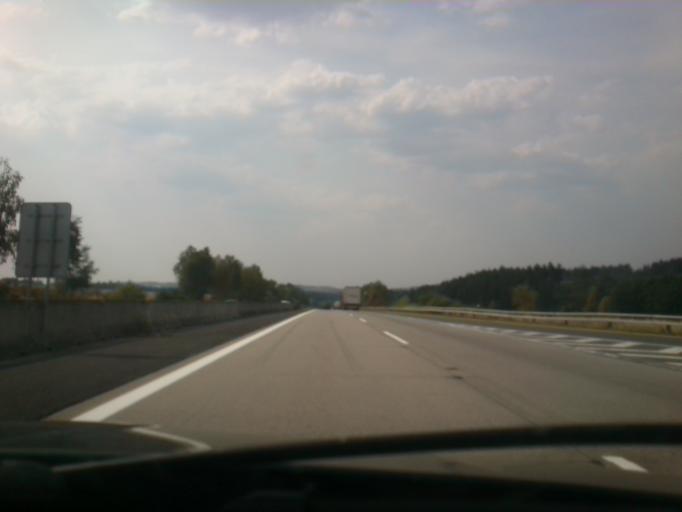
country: CZ
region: Central Bohemia
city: Divisov
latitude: 49.8034
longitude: 14.9033
